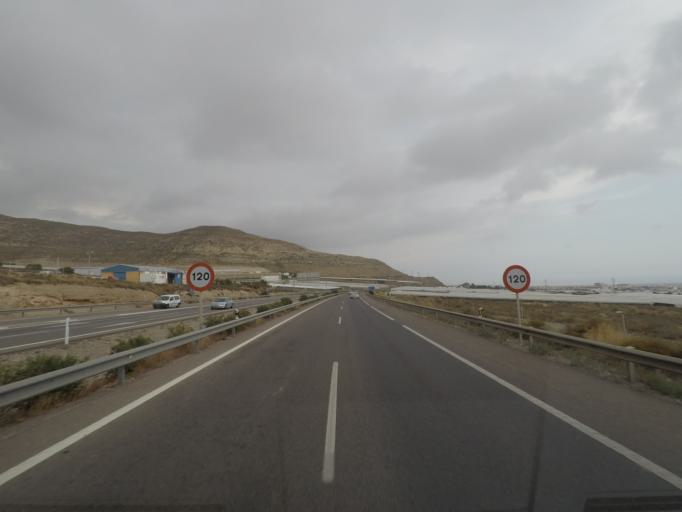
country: ES
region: Andalusia
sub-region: Provincia de Almeria
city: Vicar
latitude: 36.8137
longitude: -2.6481
